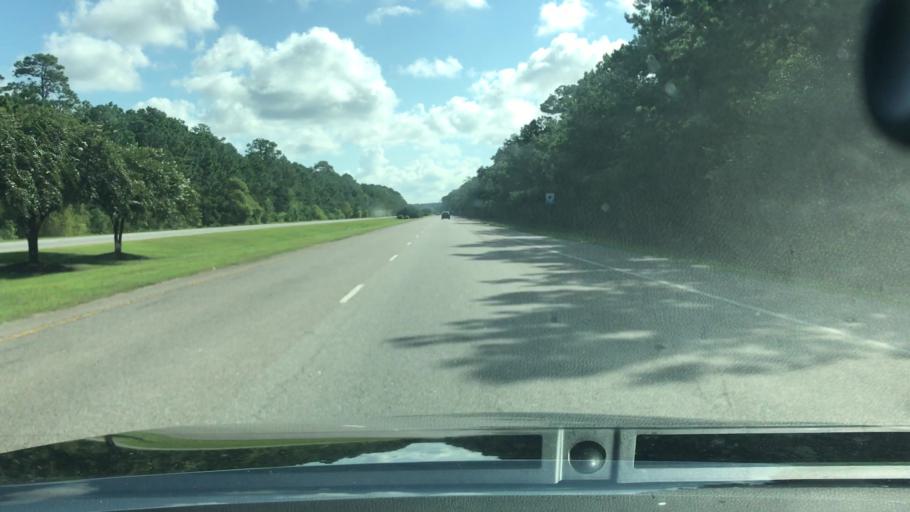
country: US
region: South Carolina
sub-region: Beaufort County
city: Hilton Head Island
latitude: 32.1972
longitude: -80.7592
